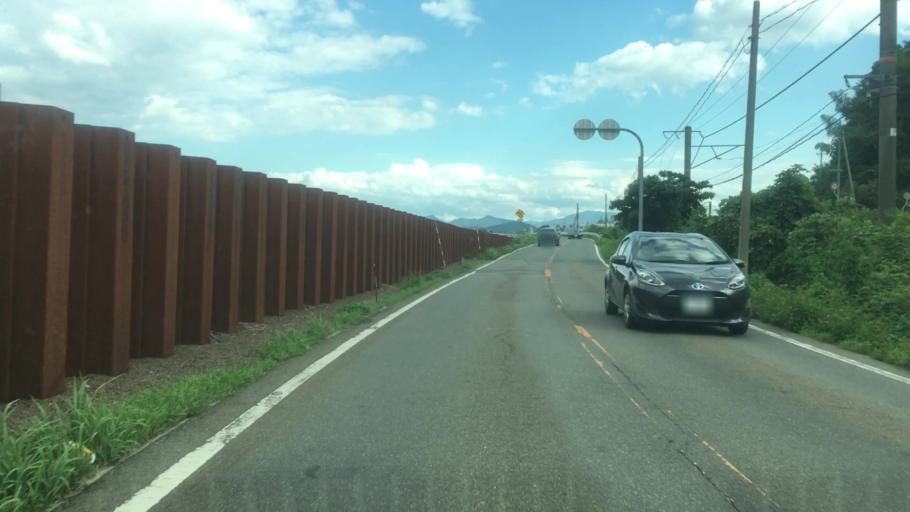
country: JP
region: Hyogo
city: Toyooka
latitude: 35.5757
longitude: 134.8044
